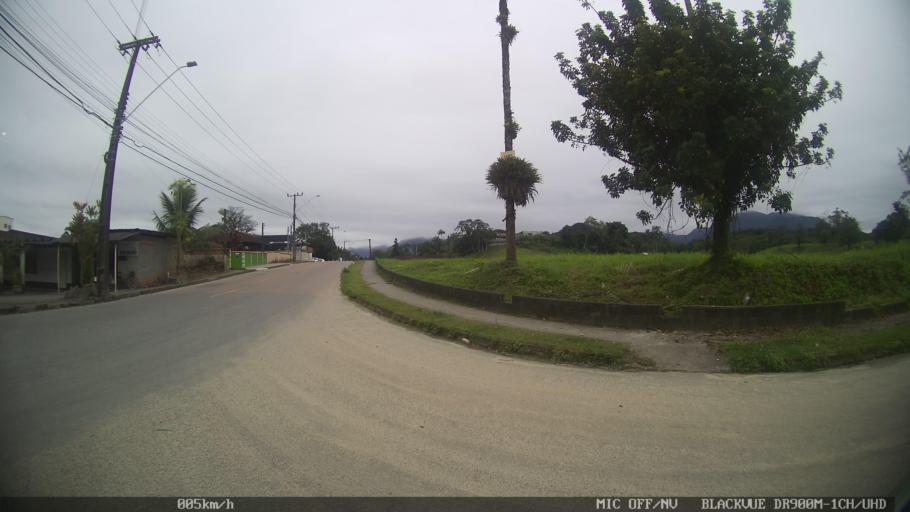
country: BR
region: Santa Catarina
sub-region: Joinville
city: Joinville
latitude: -26.2775
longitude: -48.9092
